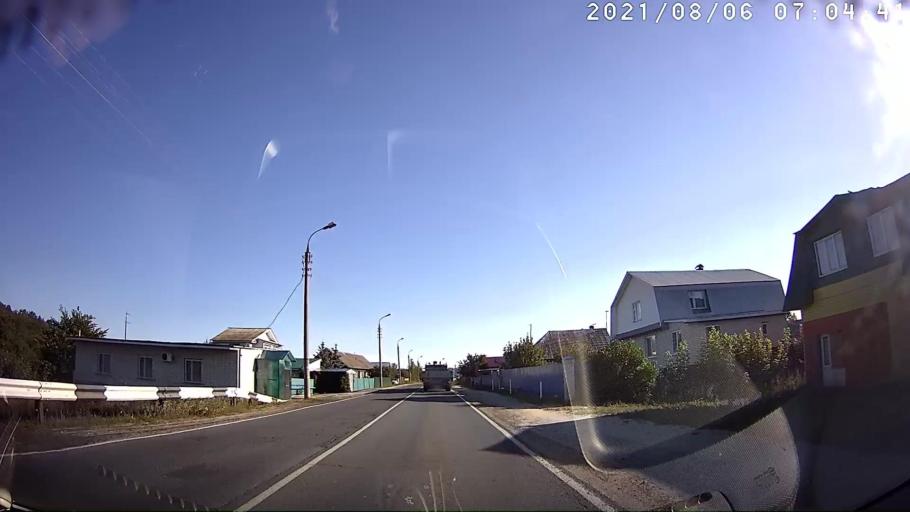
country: RU
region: Mariy-El
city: Yoshkar-Ola
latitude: 56.5488
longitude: 47.9832
